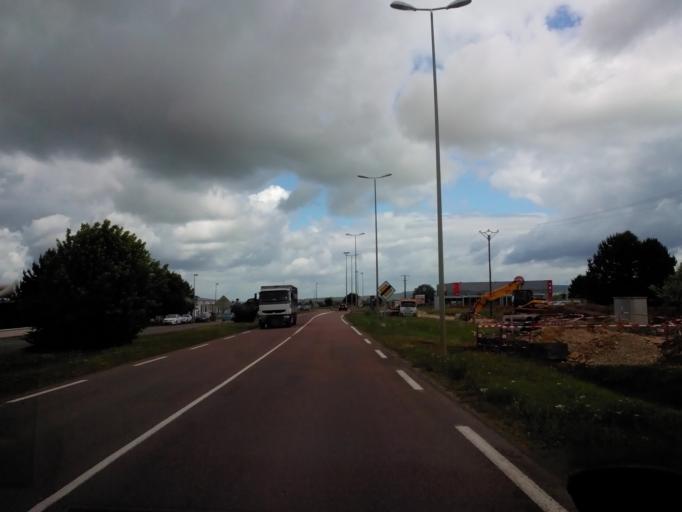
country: FR
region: Bourgogne
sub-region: Departement de la Cote-d'Or
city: Chatillon-sur-Seine
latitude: 47.8770
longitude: 4.5679
